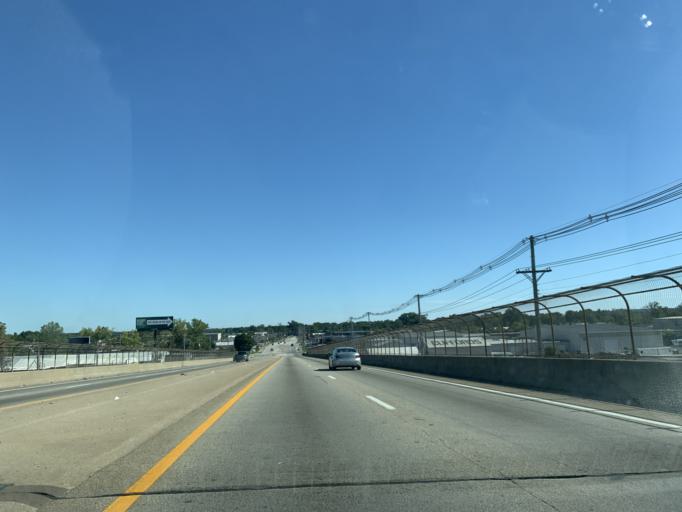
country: US
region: Kentucky
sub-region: Jefferson County
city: Audubon Park
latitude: 38.1908
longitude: -85.7046
